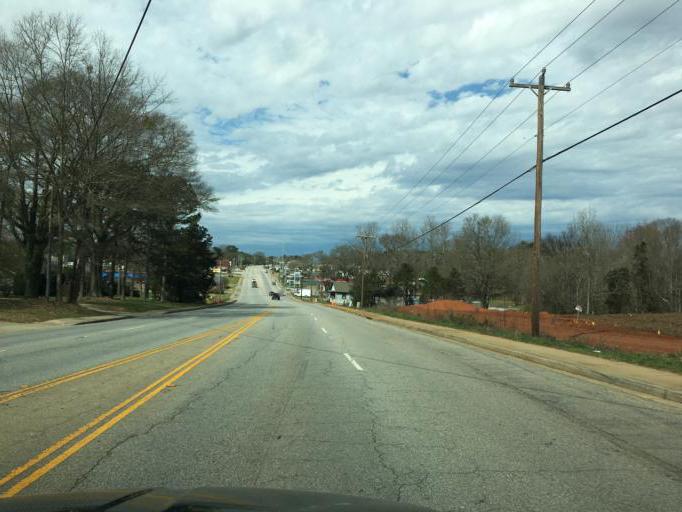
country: US
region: South Carolina
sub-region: Greenville County
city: Fountain Inn
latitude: 34.7010
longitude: -82.2138
